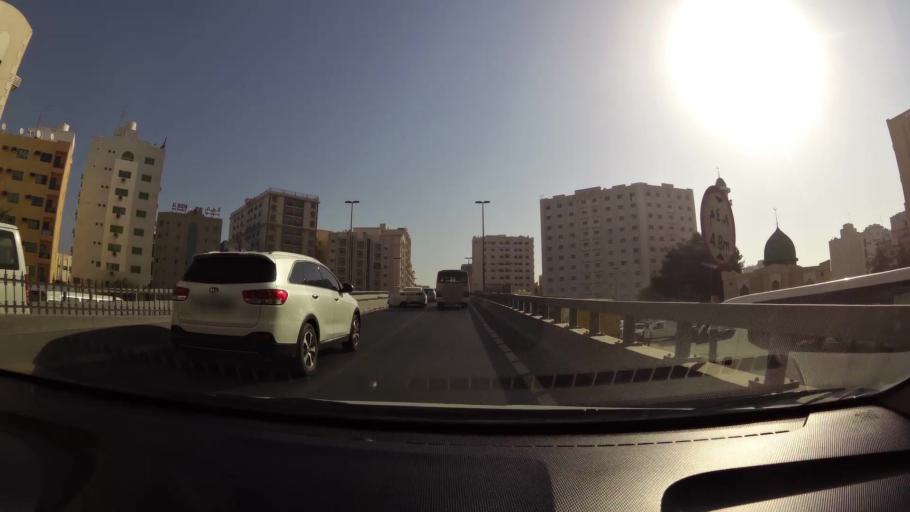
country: AE
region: Ash Shariqah
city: Sharjah
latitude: 25.3680
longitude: 55.3955
